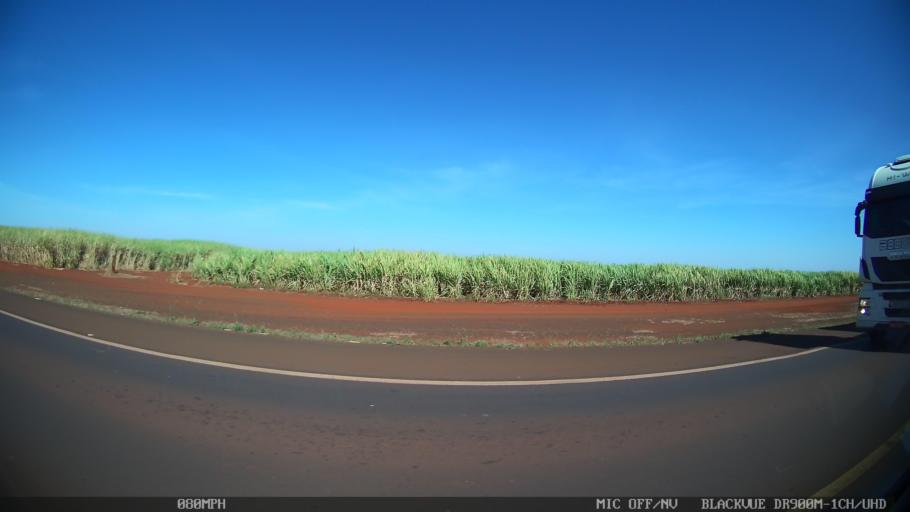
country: BR
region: Sao Paulo
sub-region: Guaira
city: Guaira
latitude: -20.4444
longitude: -48.2797
